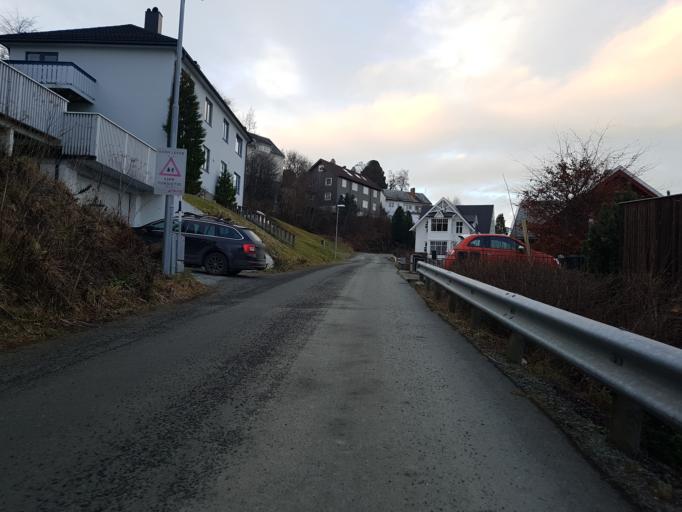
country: NO
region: Sor-Trondelag
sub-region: Trondheim
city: Trondheim
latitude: 63.4220
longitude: 10.3714
